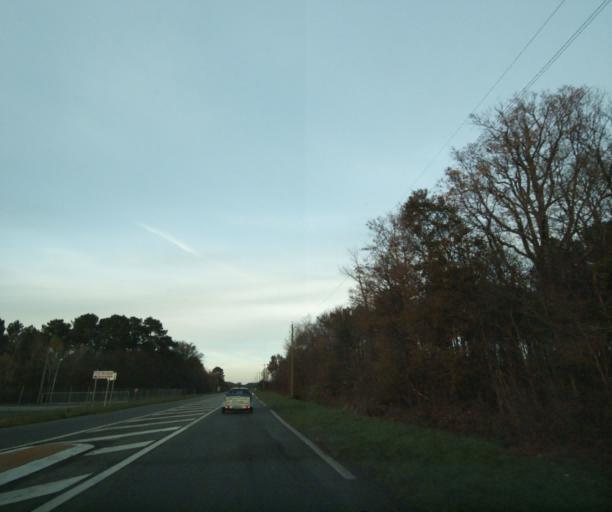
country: FR
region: Aquitaine
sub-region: Departement de la Gironde
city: Bazas
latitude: 44.4628
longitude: -0.2308
